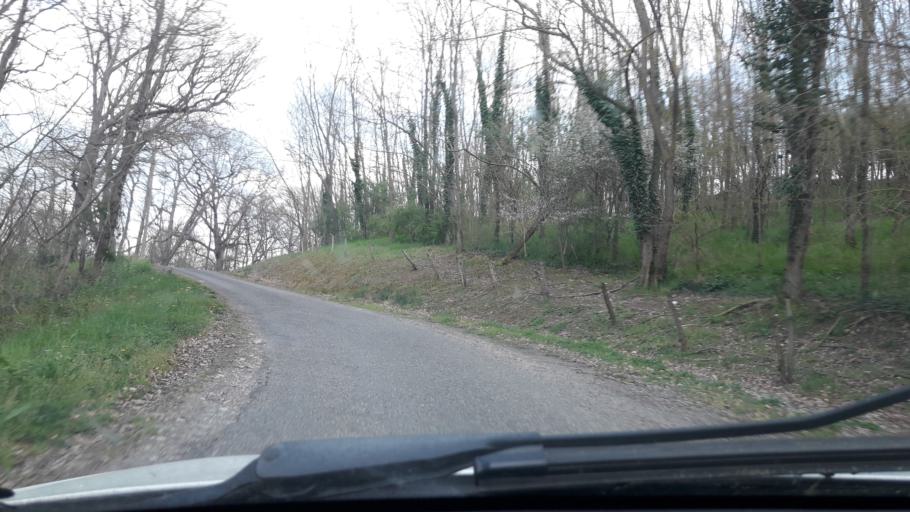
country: FR
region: Midi-Pyrenees
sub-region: Departement de la Haute-Garonne
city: Montesquieu-Volvestre
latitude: 43.2167
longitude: 1.2252
